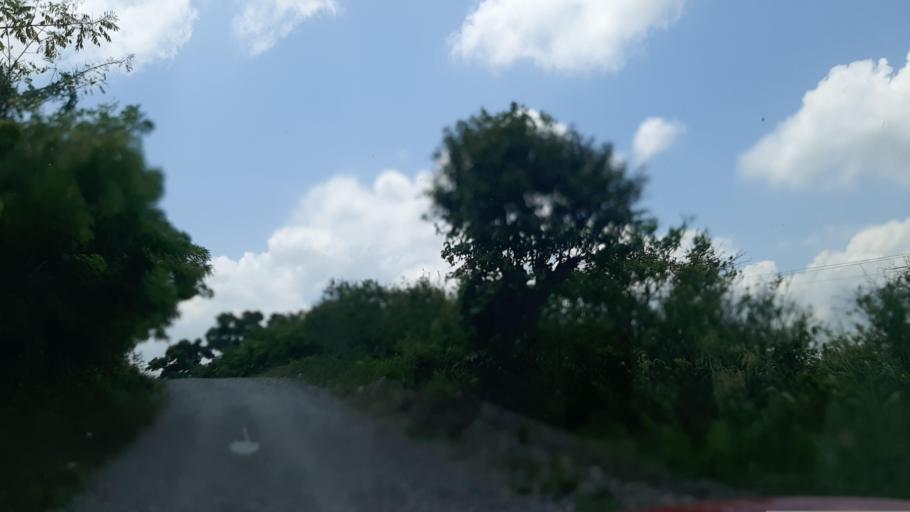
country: MX
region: Veracruz
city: Agua Dulce
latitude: 20.4099
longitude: -97.2827
